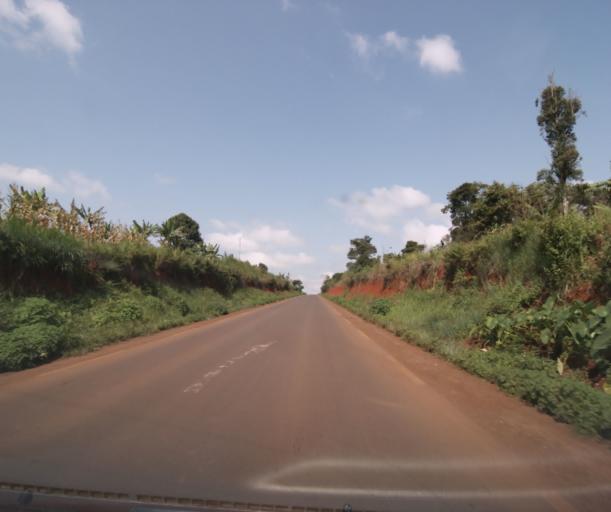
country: CM
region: West
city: Bansoa
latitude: 5.4977
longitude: 10.2313
